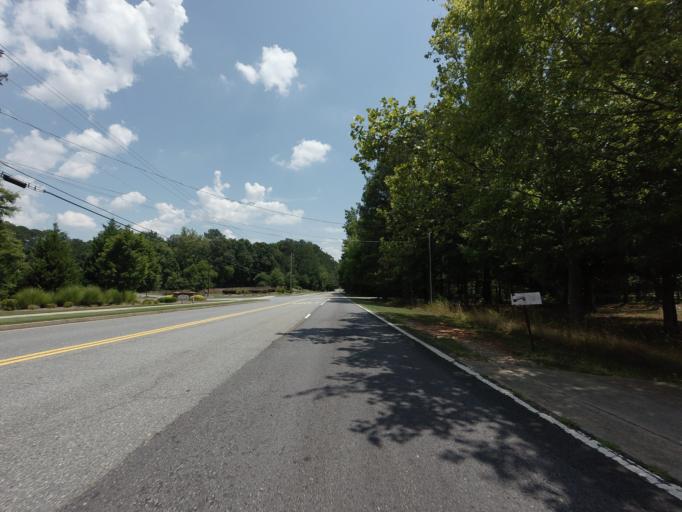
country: US
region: Georgia
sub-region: Fulton County
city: Johns Creek
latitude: 34.0525
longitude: -84.1987
